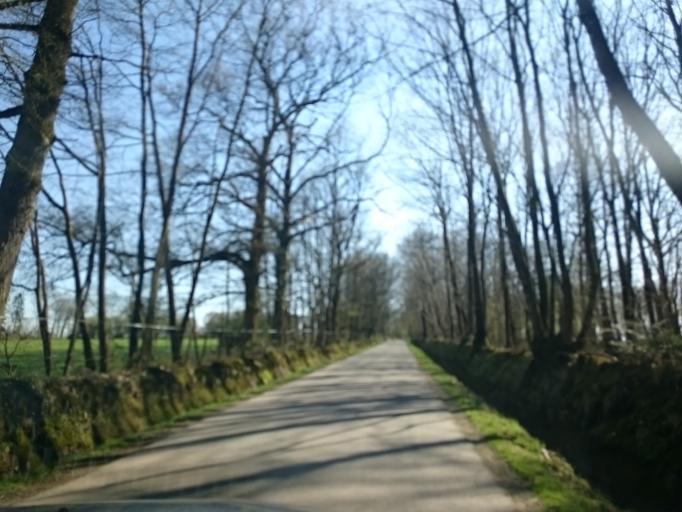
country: FR
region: Brittany
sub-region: Departement d'Ille-et-Vilaine
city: Orgeres
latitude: 47.9712
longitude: -1.6761
